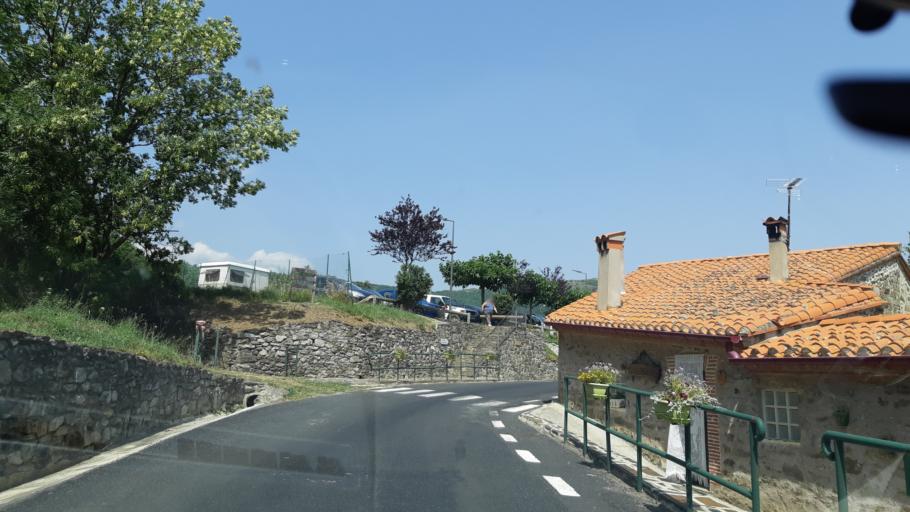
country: FR
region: Languedoc-Roussillon
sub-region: Departement des Pyrenees-Orientales
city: els Banys d'Arles
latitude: 42.5241
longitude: 2.6317
